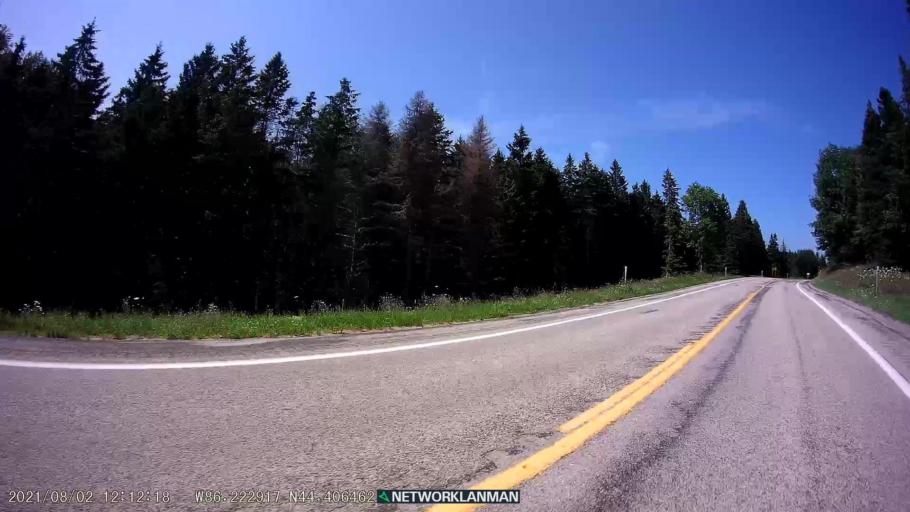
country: US
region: Michigan
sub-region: Manistee County
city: Manistee
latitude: 44.4068
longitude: -86.2231
